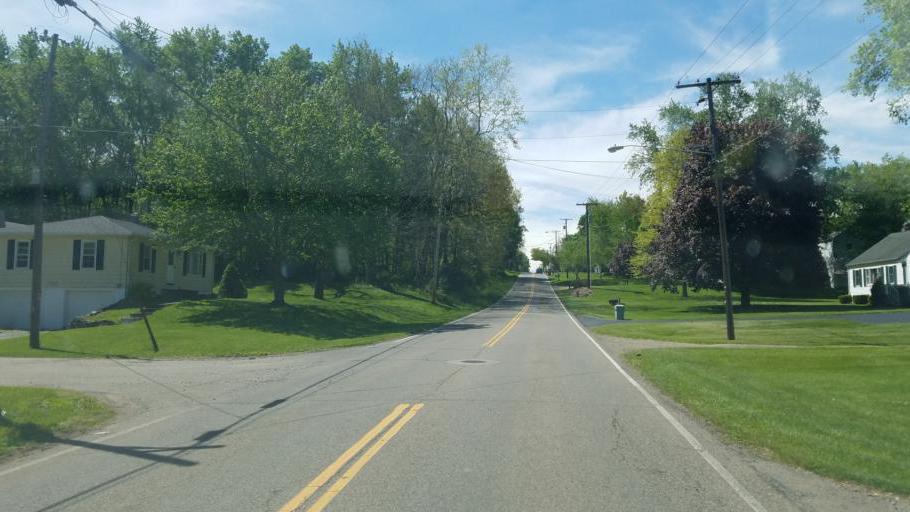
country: US
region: Ohio
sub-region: Knox County
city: Mount Vernon
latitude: 40.4158
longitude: -82.4950
